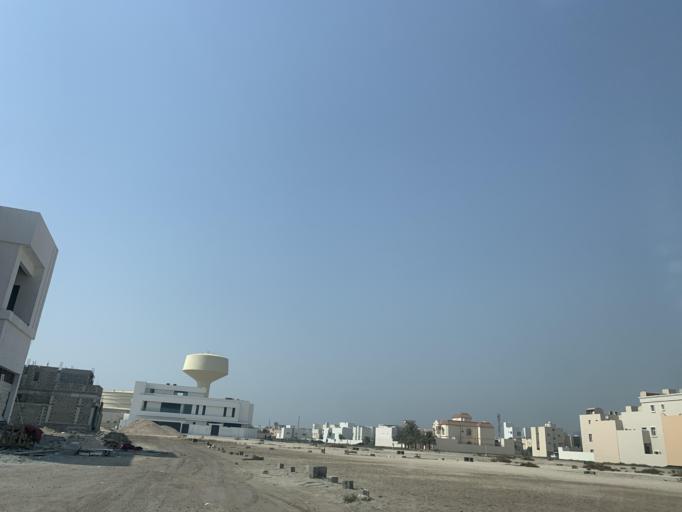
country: BH
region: Manama
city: Jidd Hafs
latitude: 26.2052
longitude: 50.5271
